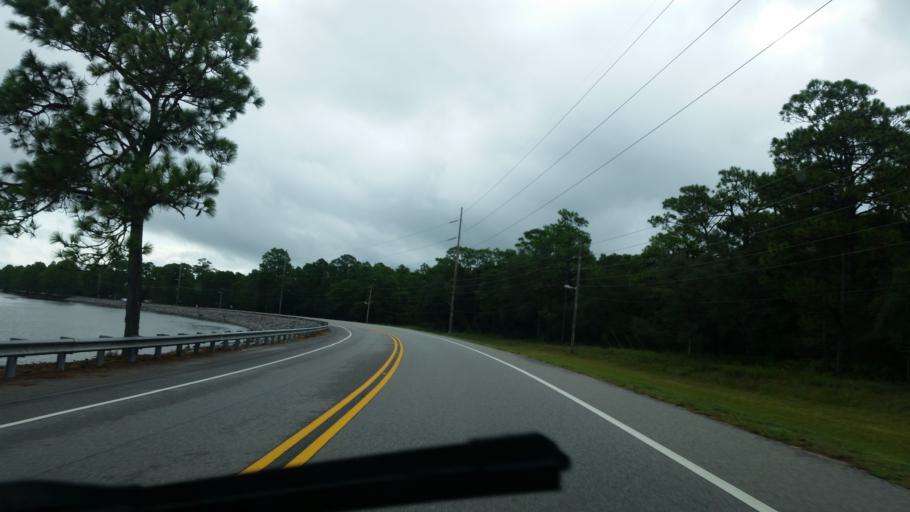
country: US
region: Alabama
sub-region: Baldwin County
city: Gulf Shores
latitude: 30.2795
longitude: -87.6529
